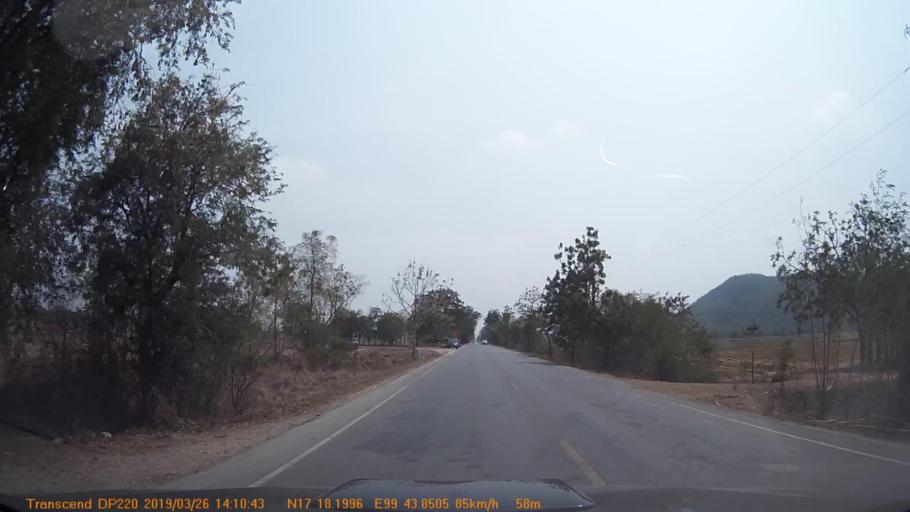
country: TH
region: Sukhothai
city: Sawankhalok
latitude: 17.3028
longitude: 99.7307
